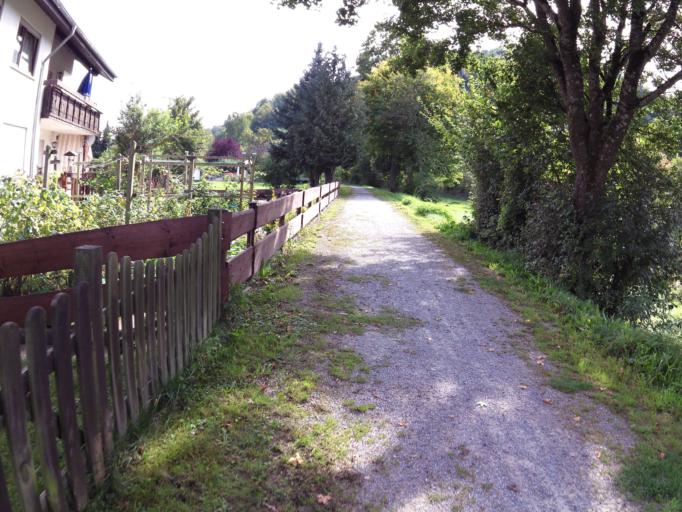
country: DE
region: Baden-Wuerttemberg
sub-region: Freiburg Region
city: Oberndorf
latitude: 48.3087
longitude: 8.5719
